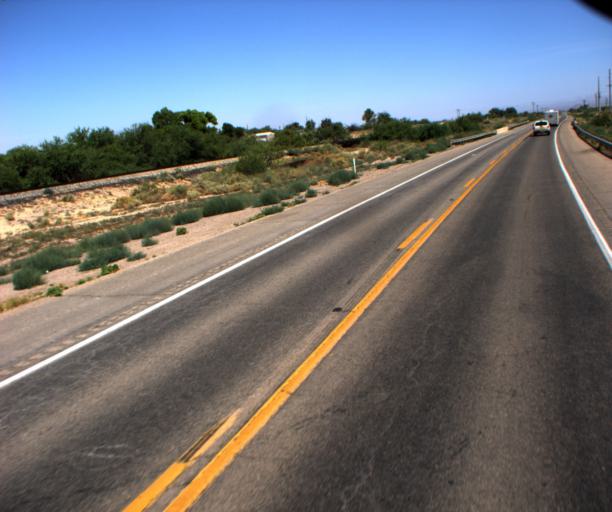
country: US
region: Arizona
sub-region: Graham County
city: Pima
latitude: 32.9440
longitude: -109.9097
